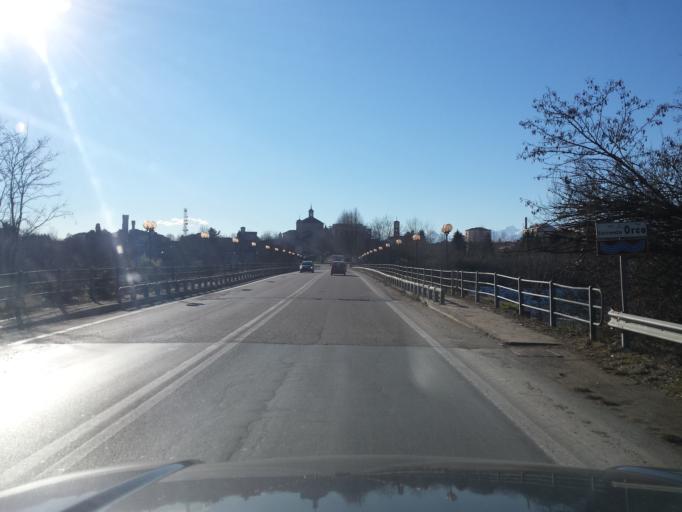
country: IT
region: Piedmont
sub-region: Provincia di Torino
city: Rivarolo Canavese
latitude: 45.3357
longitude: 7.7323
